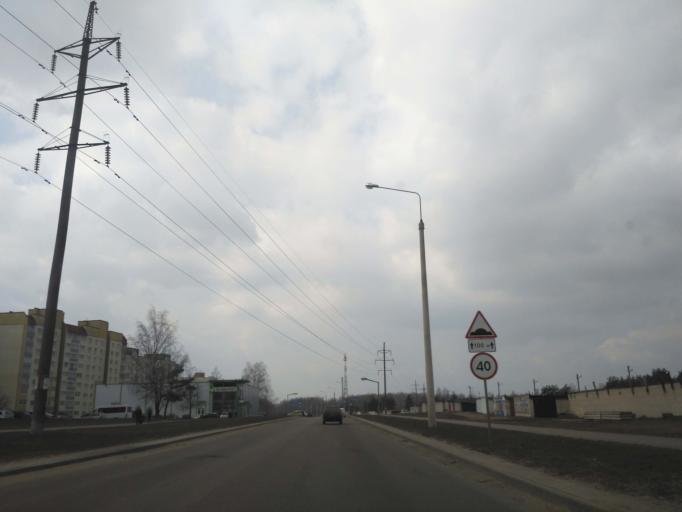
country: BY
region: Minsk
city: Horad Barysaw
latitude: 54.2162
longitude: 28.4747
